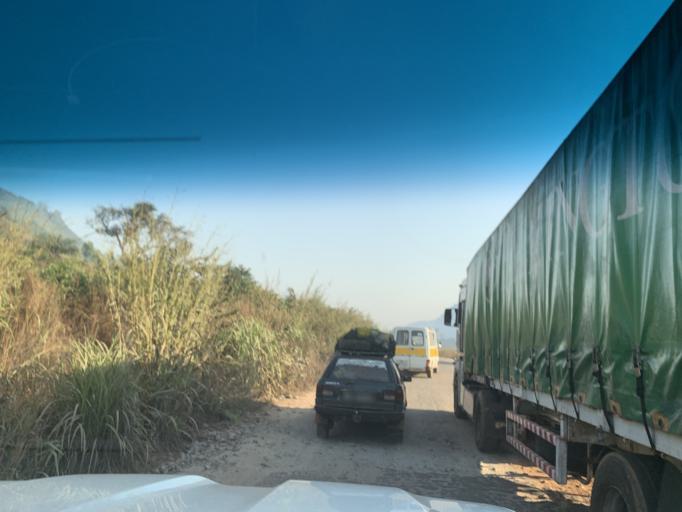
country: GN
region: Kindia
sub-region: Coyah
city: Coyah
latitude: 9.7594
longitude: -13.3518
